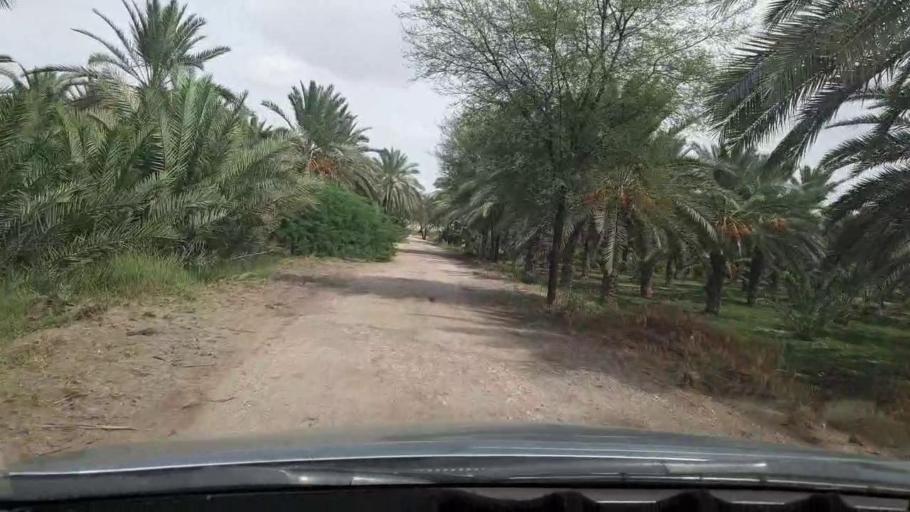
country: PK
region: Sindh
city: Khairpur
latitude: 27.4734
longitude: 68.8509
